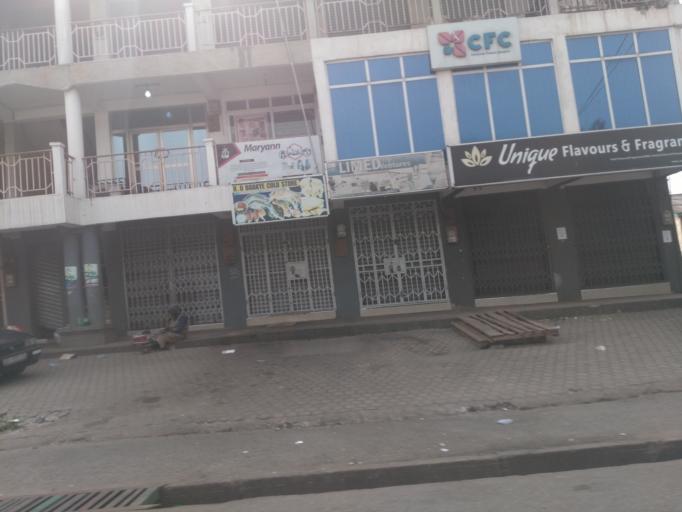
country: GH
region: Ashanti
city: Kumasi
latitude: 6.6932
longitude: -1.6194
